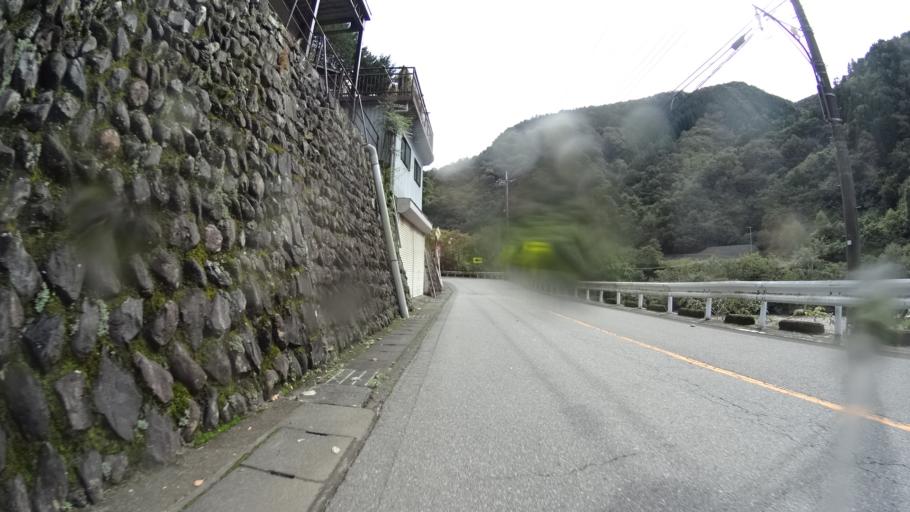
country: JP
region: Yamanashi
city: Otsuki
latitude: 35.7793
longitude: 138.9804
